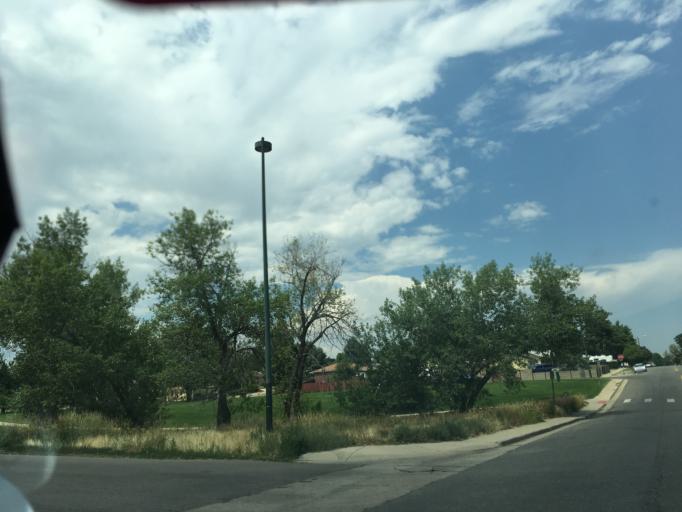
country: US
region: Colorado
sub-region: Arapahoe County
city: Sheridan
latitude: 39.6846
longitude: -105.0344
